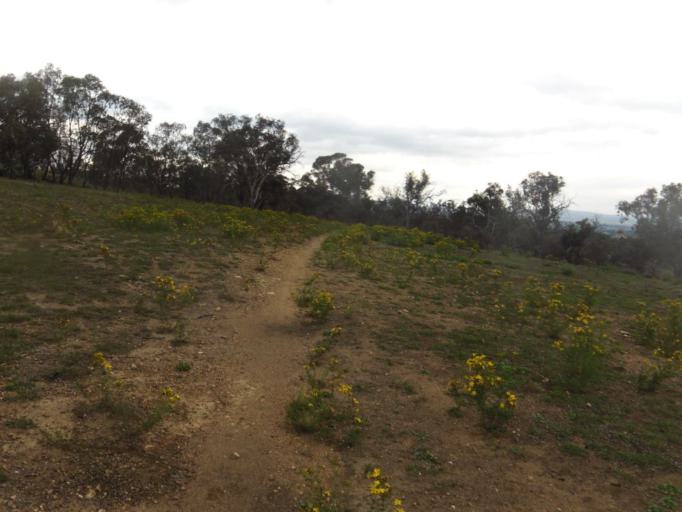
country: AU
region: Australian Capital Territory
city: Forrest
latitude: -35.3477
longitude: 149.1344
